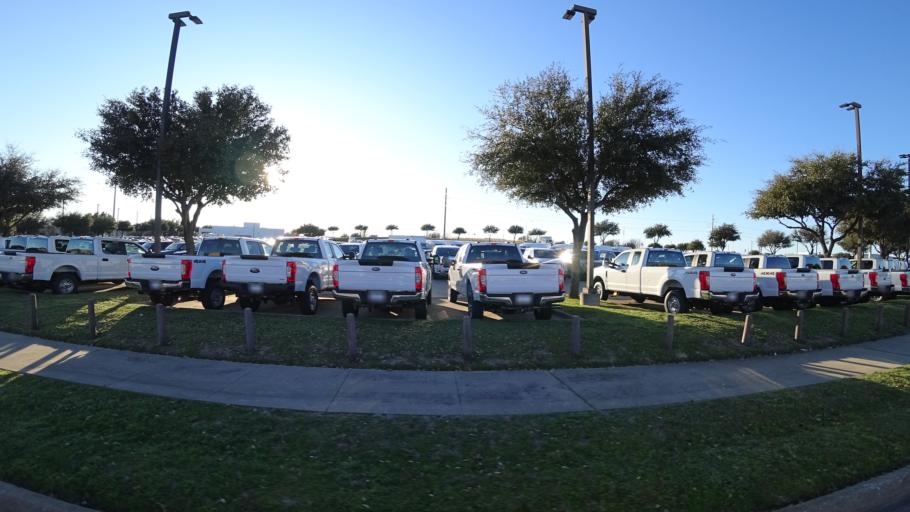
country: US
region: Texas
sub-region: Denton County
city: Lewisville
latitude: 33.0555
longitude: -97.0079
